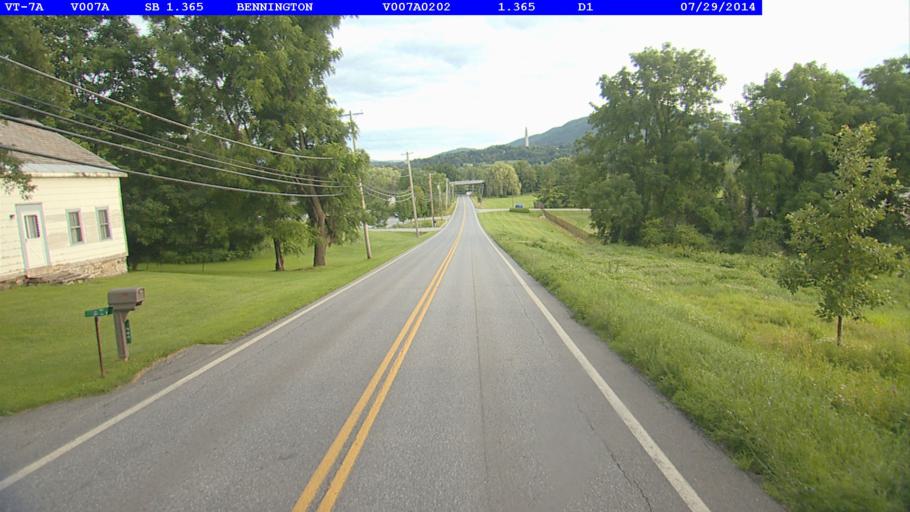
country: US
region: Vermont
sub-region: Bennington County
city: Bennington
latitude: 42.9092
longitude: -73.2115
